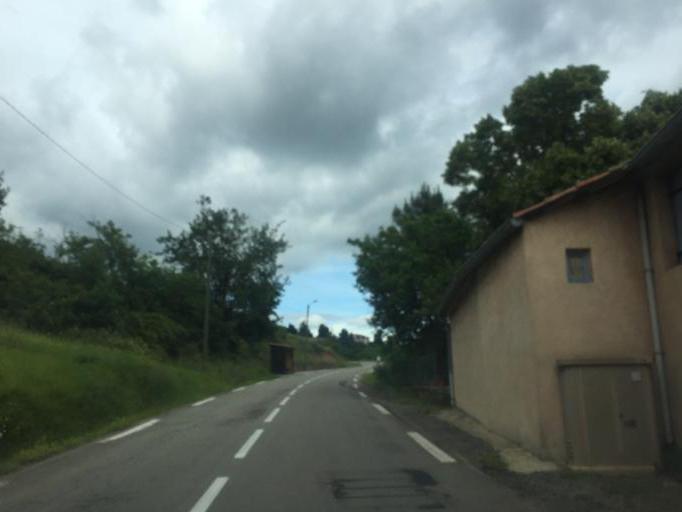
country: FR
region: Rhone-Alpes
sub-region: Departement de l'Ardeche
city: Privas
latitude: 44.7437
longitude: 4.6079
